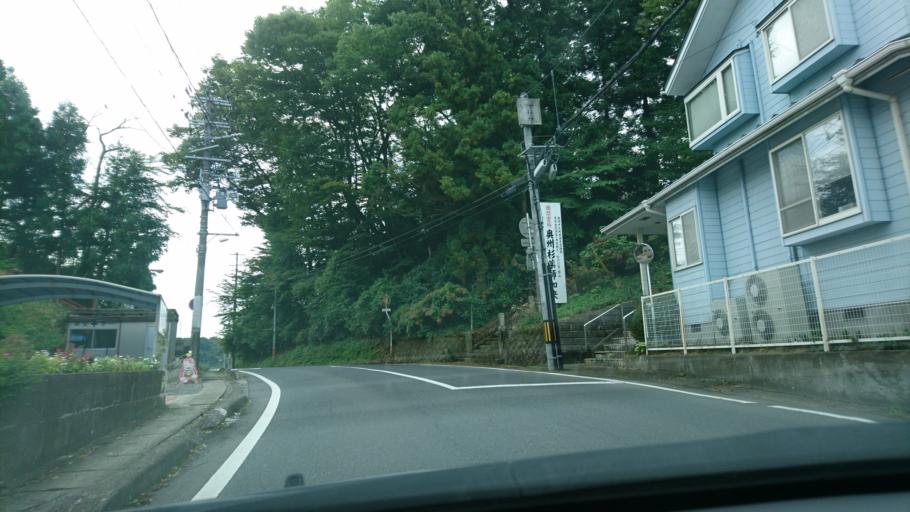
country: JP
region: Miyagi
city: Furukawa
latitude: 38.7311
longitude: 141.0187
